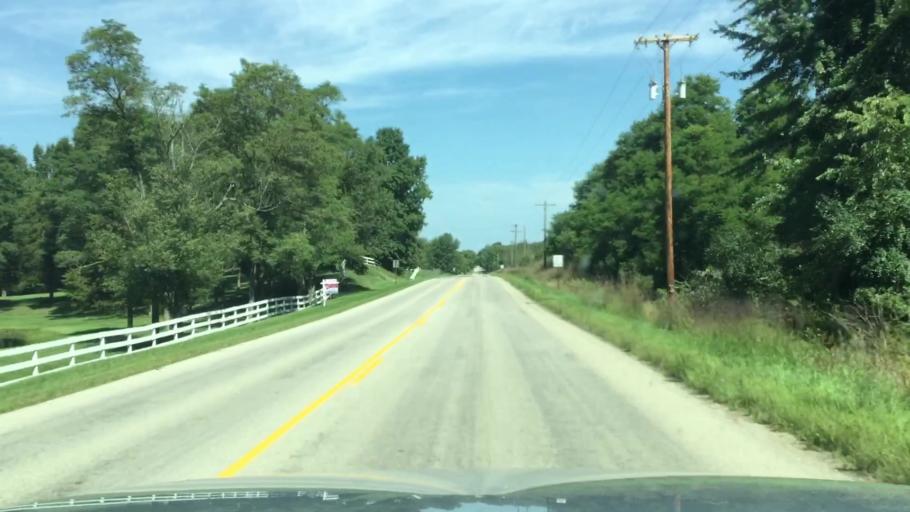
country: US
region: Michigan
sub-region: Lenawee County
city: Manitou Beach-Devils Lake
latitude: 42.0321
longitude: -84.2763
